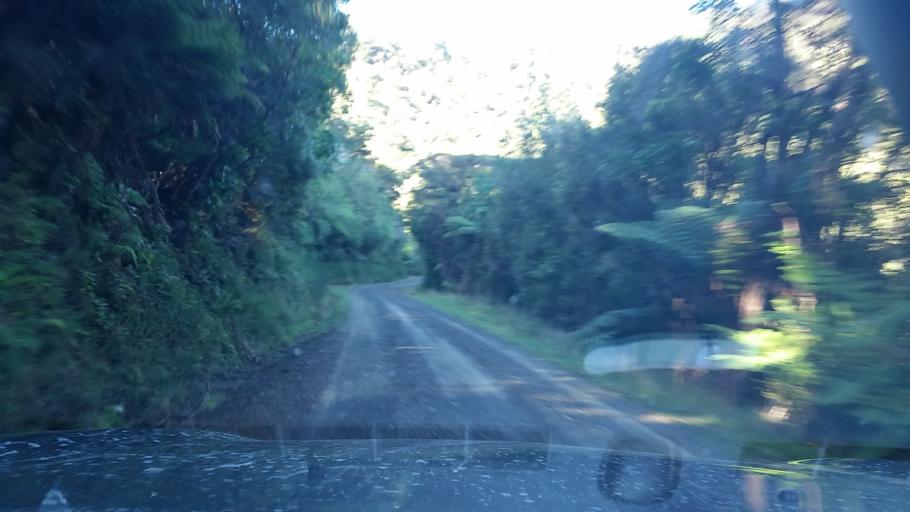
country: NZ
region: Marlborough
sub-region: Marlborough District
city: Picton
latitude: -41.1823
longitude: 173.9739
